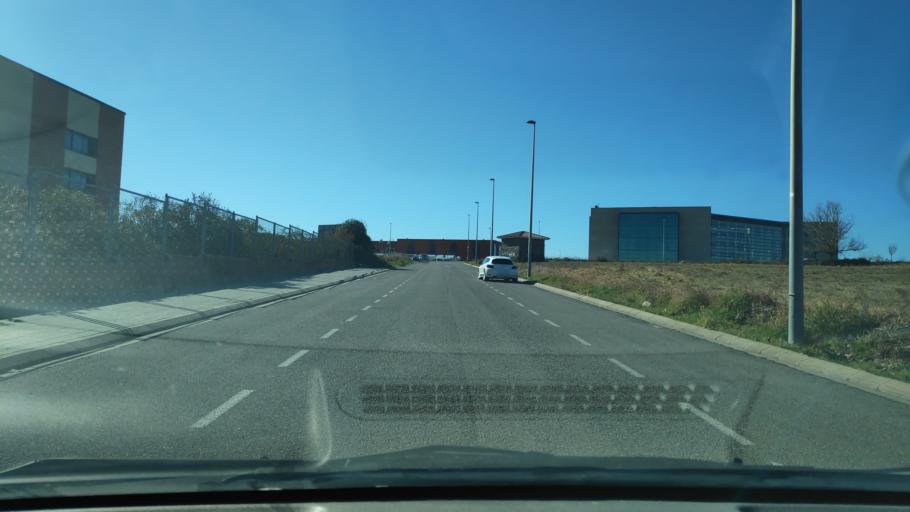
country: ES
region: Catalonia
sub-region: Provincia de Barcelona
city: Sant Quirze del Valles
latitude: 41.5383
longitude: 2.0915
